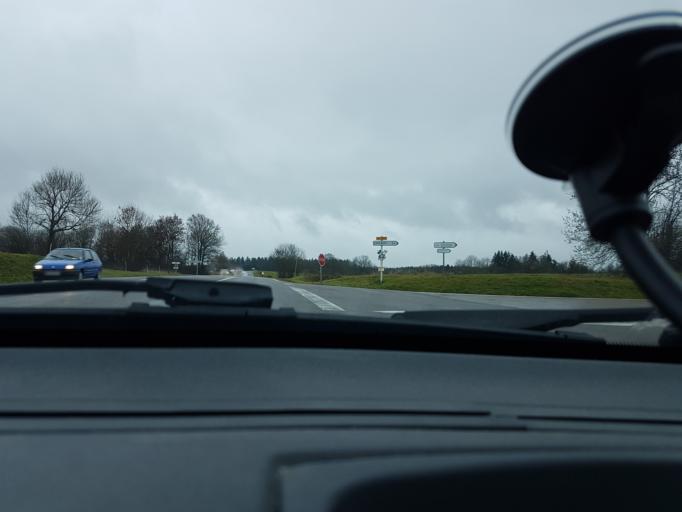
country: FR
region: Franche-Comte
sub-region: Departement du Doubs
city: Valdahon
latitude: 47.1404
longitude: 6.3808
